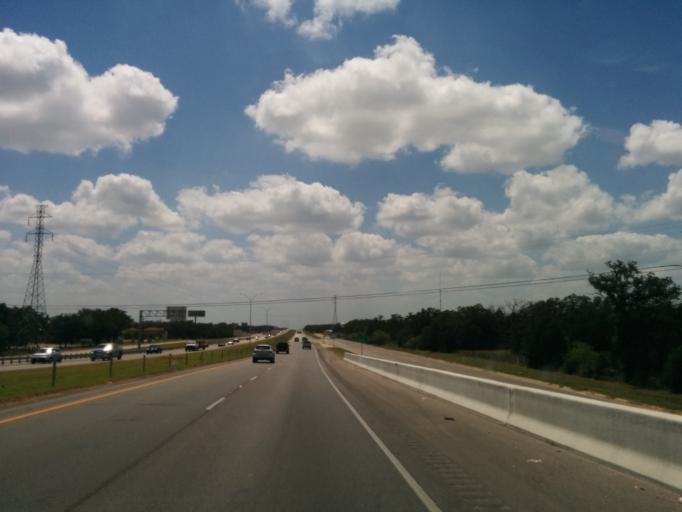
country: US
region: Texas
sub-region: Bastrop County
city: Bastrop
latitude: 30.1111
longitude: -97.3755
